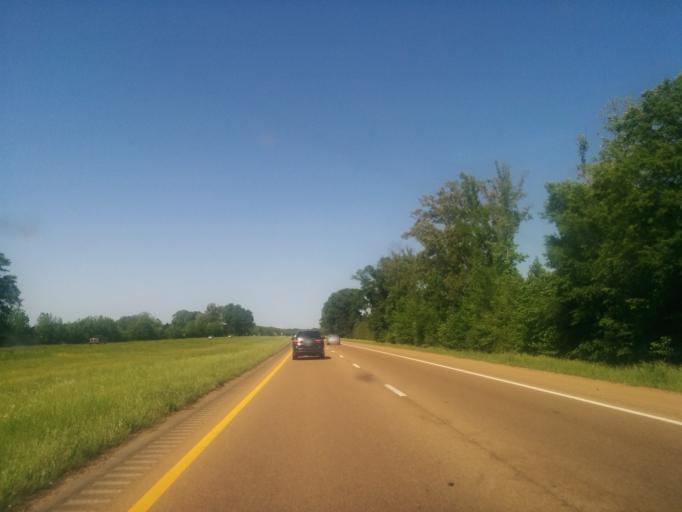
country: US
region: Mississippi
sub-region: Madison County
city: Madison
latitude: 32.4927
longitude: -90.1256
